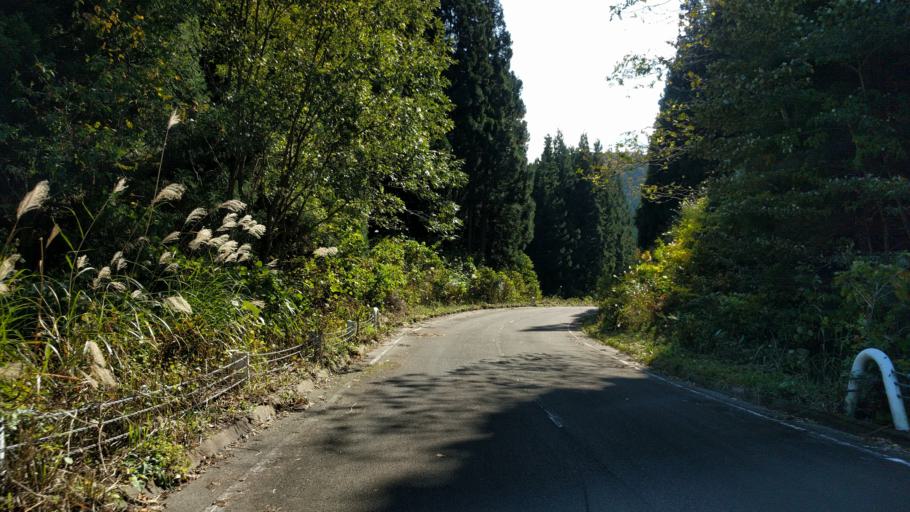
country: JP
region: Fukushima
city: Kitakata
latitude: 37.4318
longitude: 139.7818
